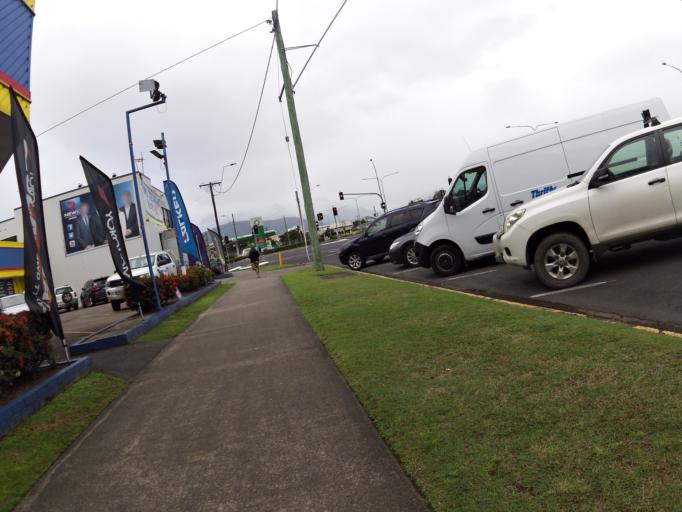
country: AU
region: Queensland
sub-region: Cairns
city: Cairns
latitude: -16.9234
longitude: 145.7662
